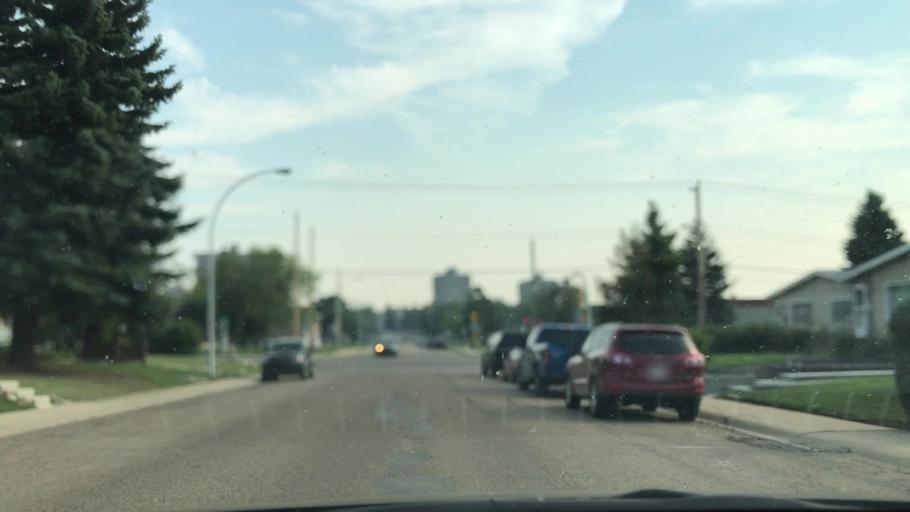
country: CA
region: Alberta
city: Edmonton
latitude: 53.4889
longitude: -113.5079
